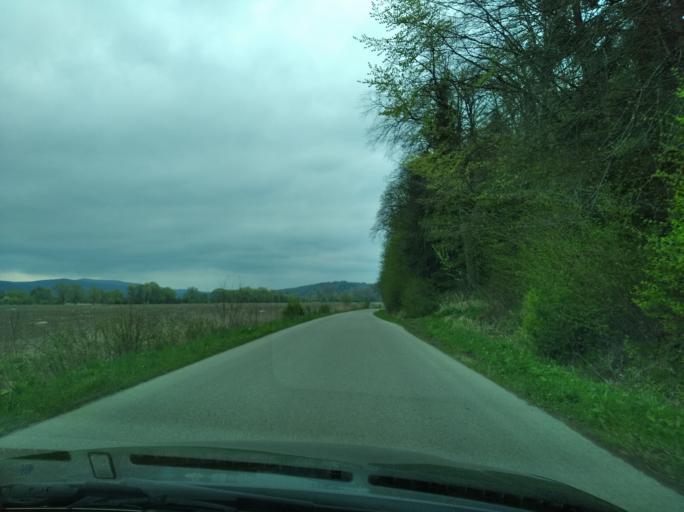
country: PL
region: Subcarpathian Voivodeship
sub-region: Powiat brzozowski
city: Dydnia
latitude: 49.6798
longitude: 22.2440
